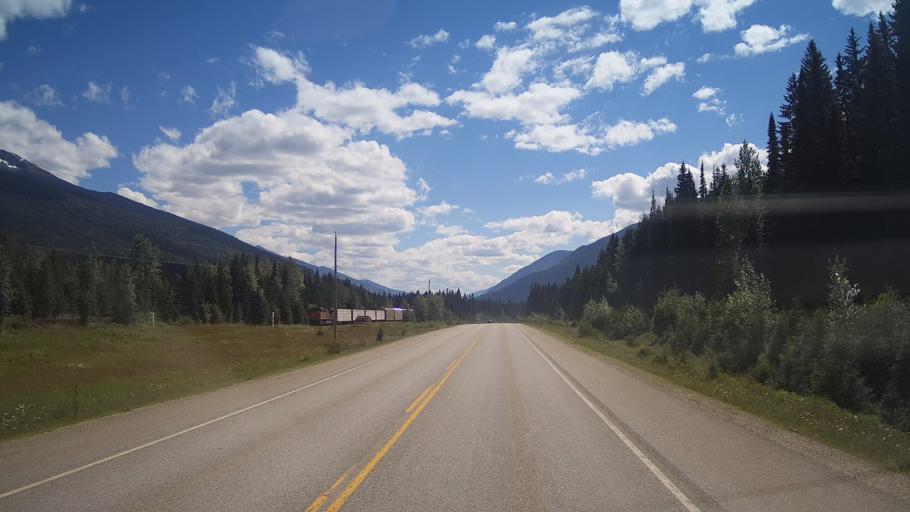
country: CA
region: Alberta
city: Jasper Park Lodge
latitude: 52.5769
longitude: -119.0975
